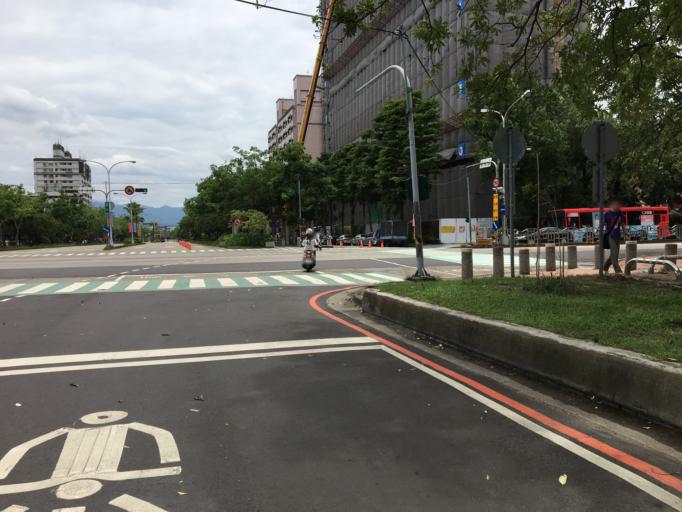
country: TW
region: Taiwan
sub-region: Taichung City
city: Taichung
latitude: 24.1240
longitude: 120.6790
